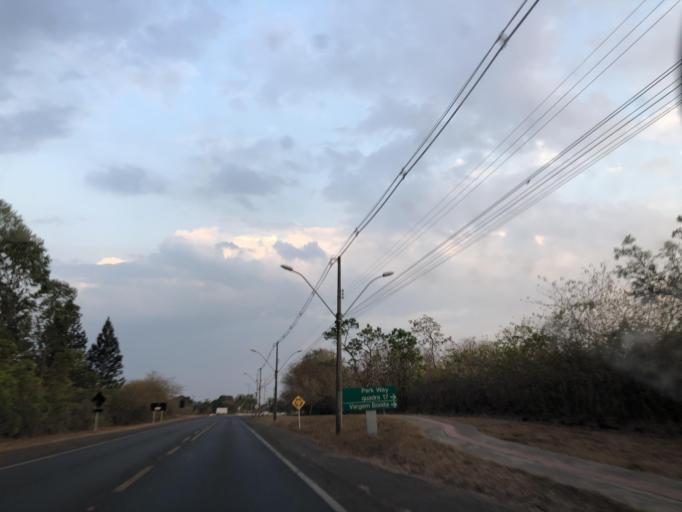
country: BR
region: Federal District
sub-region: Brasilia
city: Brasilia
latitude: -15.9084
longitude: -47.9490
